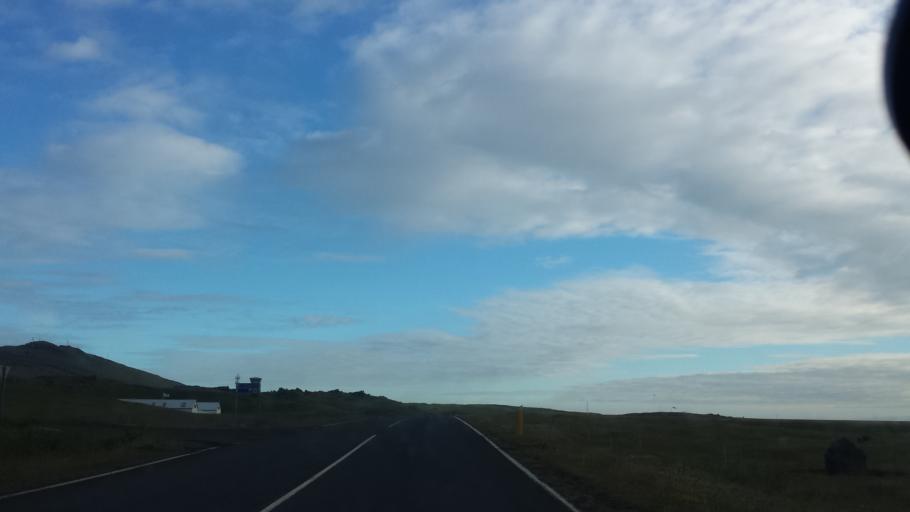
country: IS
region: South
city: Vestmannaeyjar
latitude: 63.4307
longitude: -20.2711
